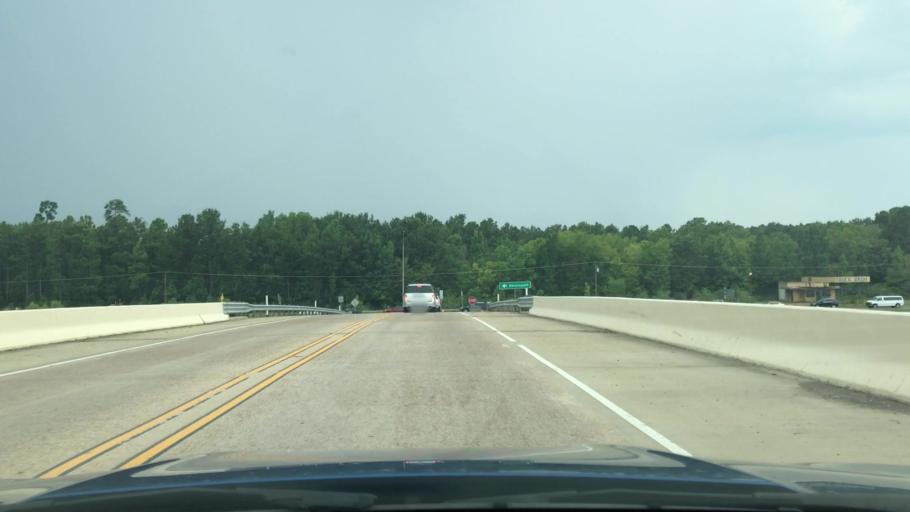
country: US
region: Texas
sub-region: Harrison County
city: Waskom
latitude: 32.4679
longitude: -94.0564
